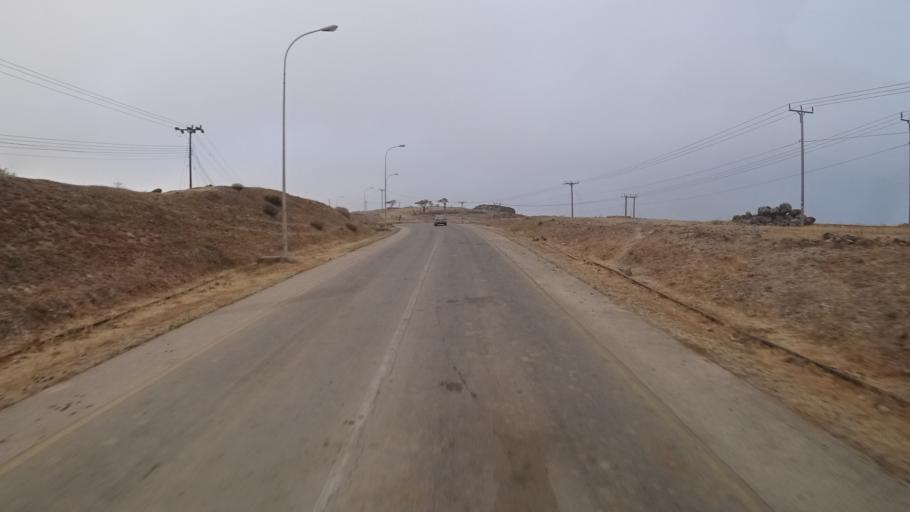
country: OM
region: Zufar
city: Salalah
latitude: 17.1293
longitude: 53.9768
